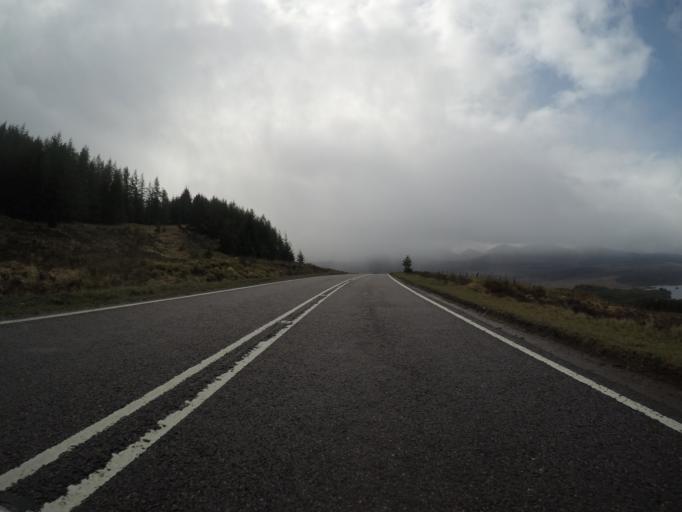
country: GB
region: Scotland
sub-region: Highland
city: Spean Bridge
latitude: 57.0857
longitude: -4.9617
